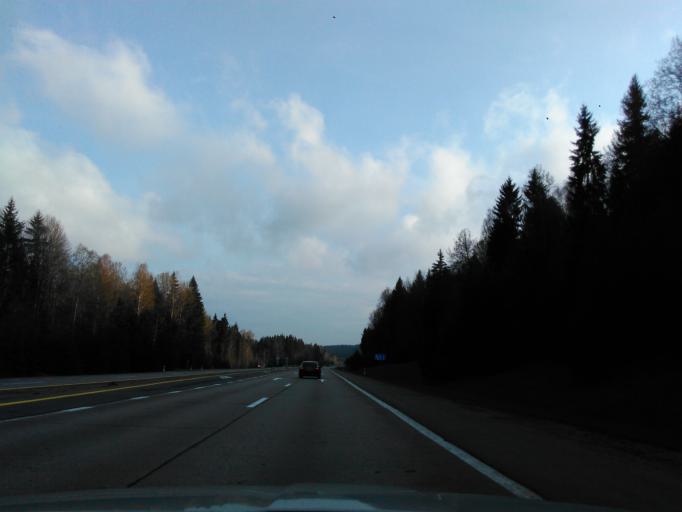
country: BY
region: Minsk
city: Lahoysk
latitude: 54.1230
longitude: 27.8073
